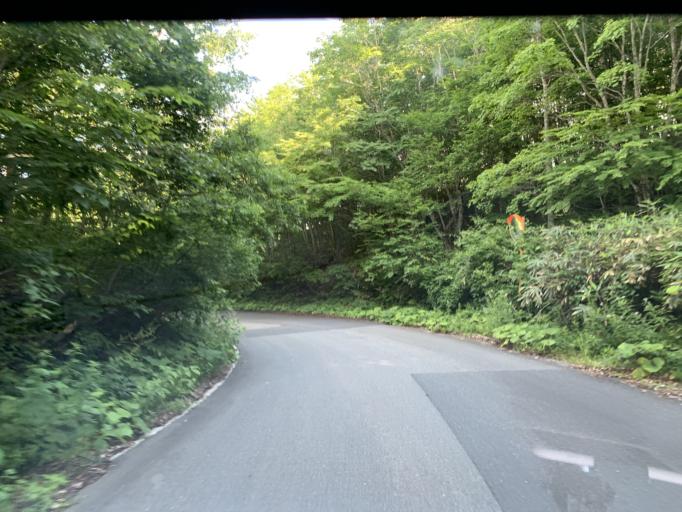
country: JP
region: Iwate
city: Ichinoseki
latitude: 38.9180
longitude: 140.8260
